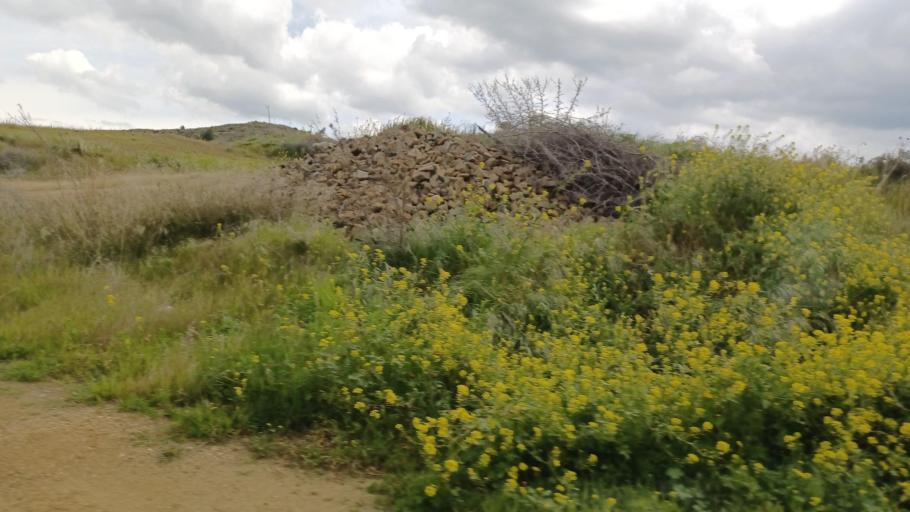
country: CY
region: Lefkosia
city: Lefka
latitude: 35.0811
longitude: 32.9259
